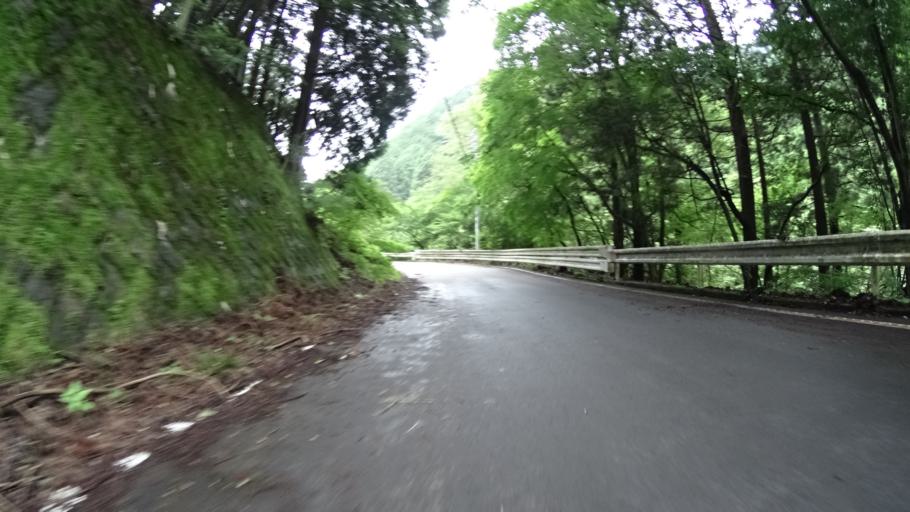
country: JP
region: Kanagawa
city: Hadano
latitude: 35.4536
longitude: 139.2121
